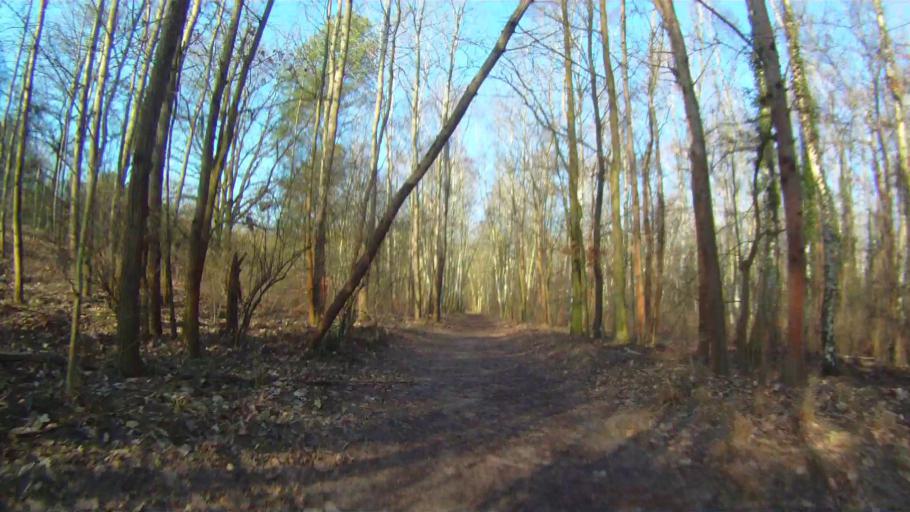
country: DE
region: Brandenburg
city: Woltersdorf
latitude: 52.4621
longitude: 13.7373
